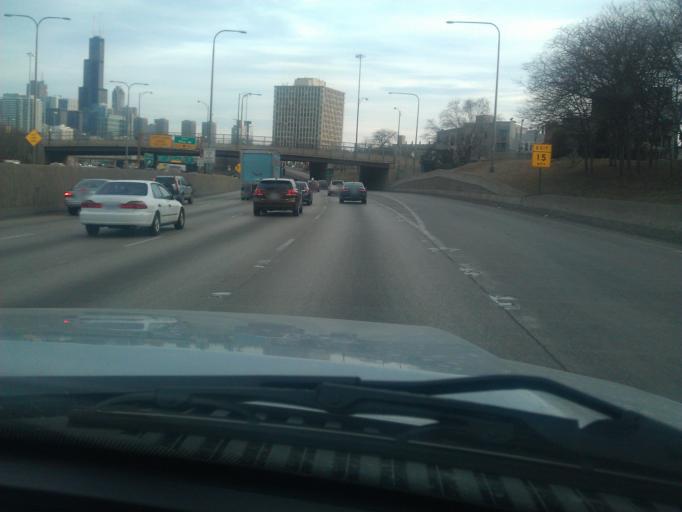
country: US
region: Illinois
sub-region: Cook County
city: Chicago
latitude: 41.8976
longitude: -87.6595
